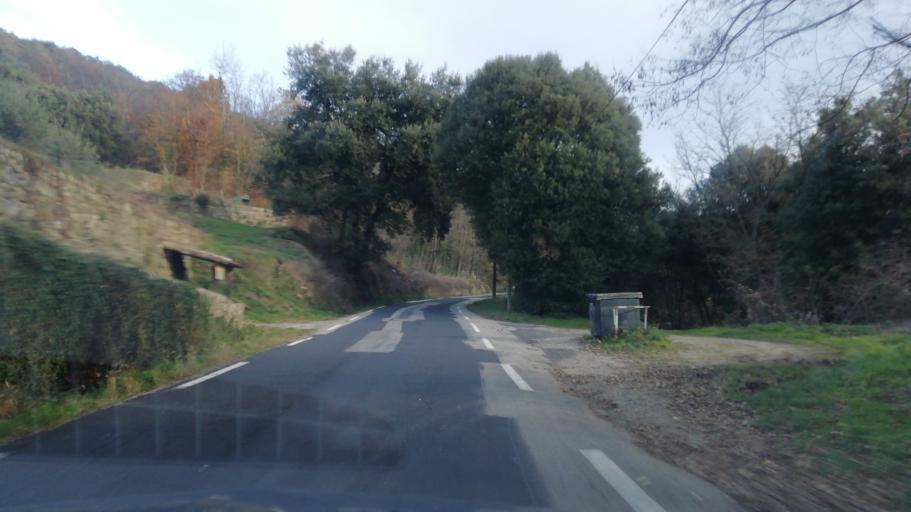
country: FR
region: Languedoc-Roussillon
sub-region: Departement du Gard
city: Lasalle
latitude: 44.0191
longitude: 3.8555
